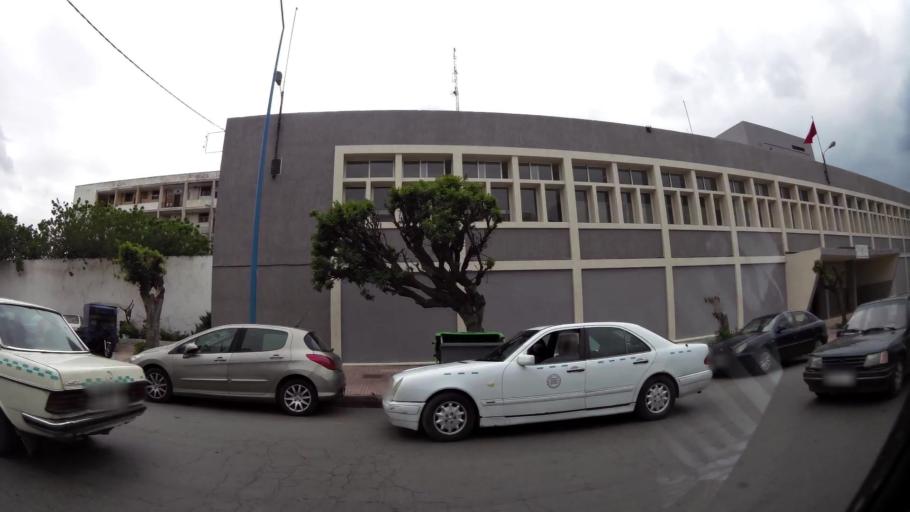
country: MA
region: Grand Casablanca
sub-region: Casablanca
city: Casablanca
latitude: 33.5944
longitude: -7.5698
